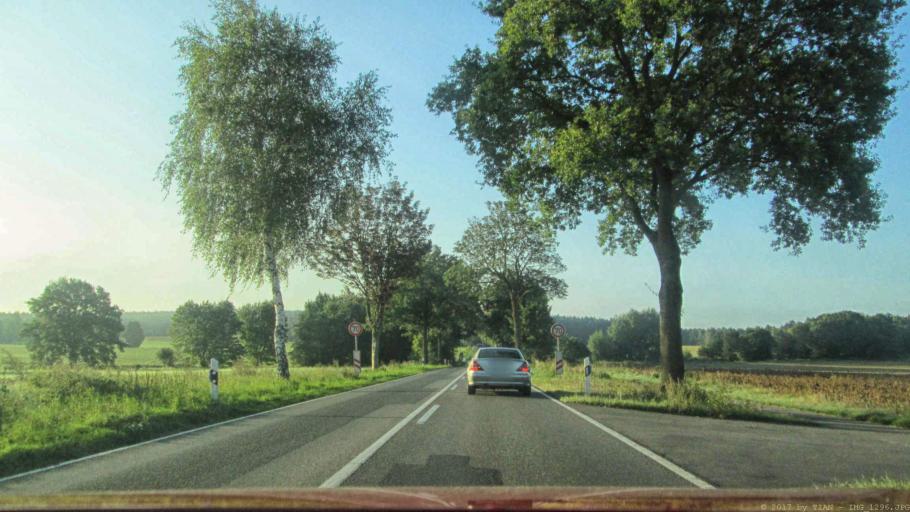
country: DE
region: Lower Saxony
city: Wieren
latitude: 52.8745
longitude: 10.6688
